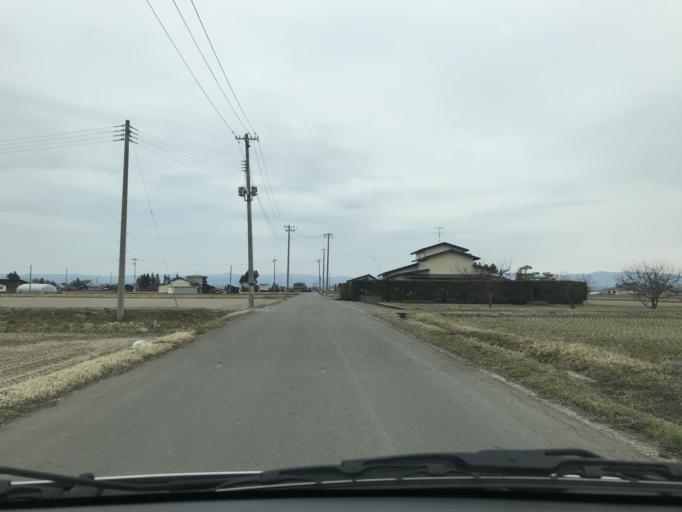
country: JP
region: Iwate
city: Mizusawa
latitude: 39.1659
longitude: 141.0985
